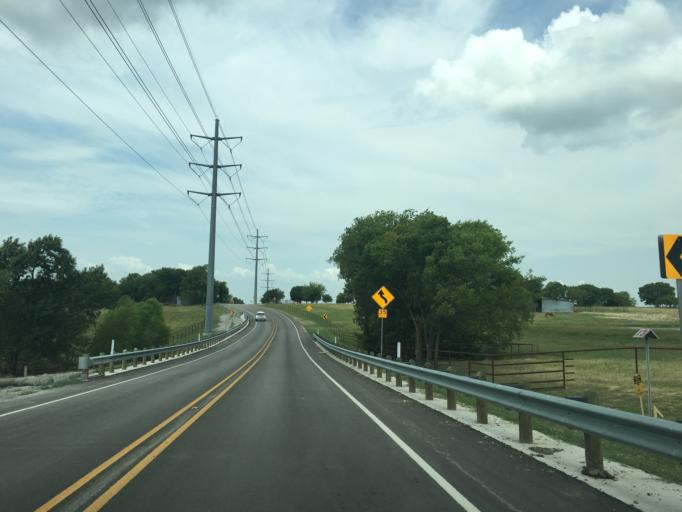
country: US
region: Texas
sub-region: Rockwall County
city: Rockwall
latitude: 32.9364
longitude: -96.4271
